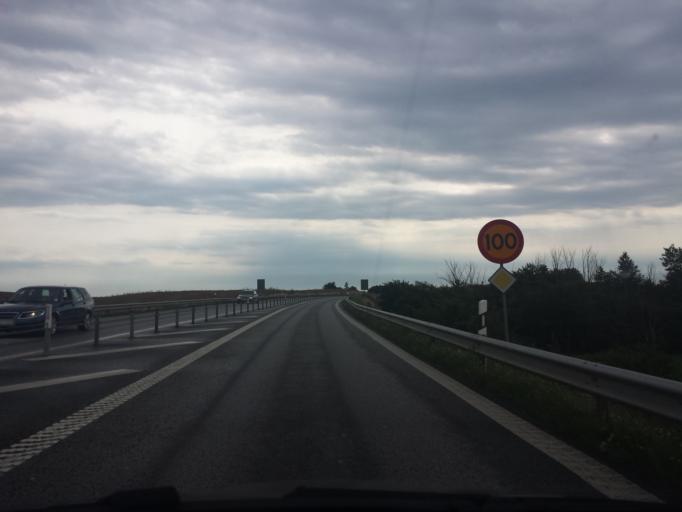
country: SE
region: Skane
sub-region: Ystads Kommun
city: Ystad
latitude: 55.4461
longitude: 13.7762
